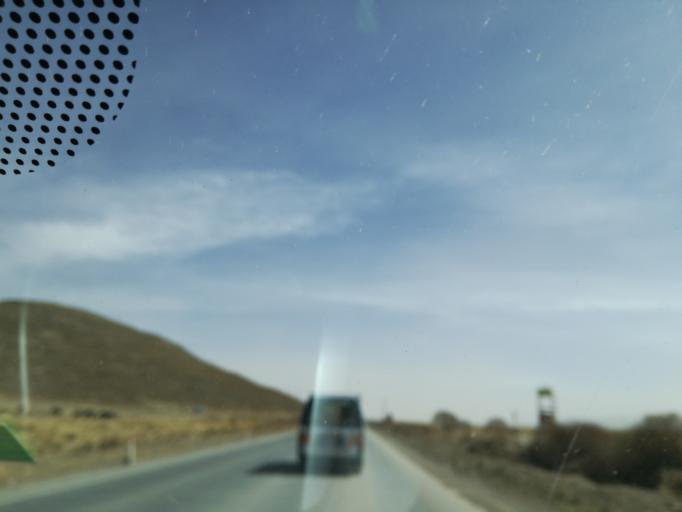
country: BO
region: Oruro
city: Oruro
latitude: -17.8867
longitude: -67.0364
